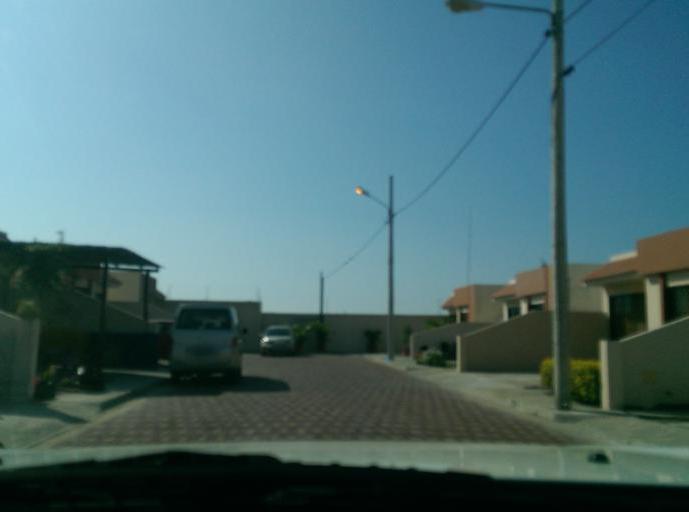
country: EC
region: Manabi
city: Manta
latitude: -0.9706
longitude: -80.7598
